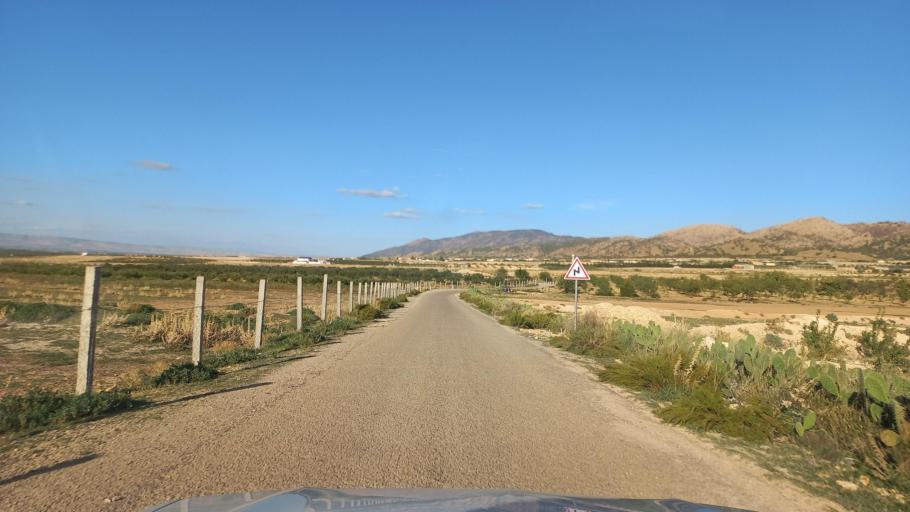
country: TN
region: Al Qasrayn
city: Sbiba
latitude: 35.3572
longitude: 9.1395
